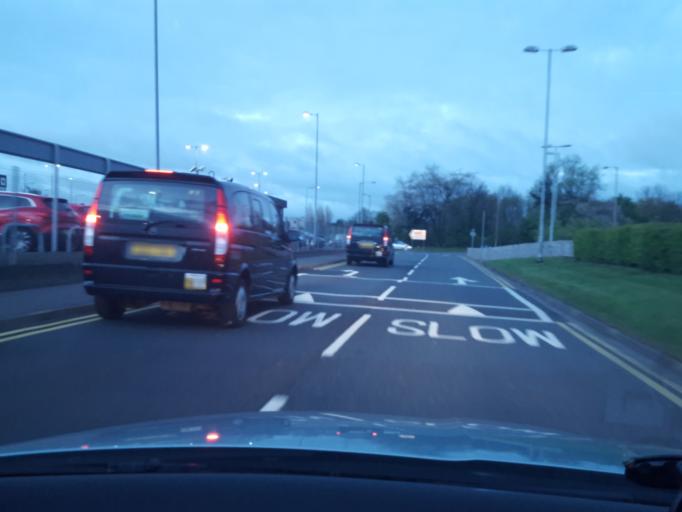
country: GB
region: Scotland
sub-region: Edinburgh
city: Ratho
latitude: 55.9459
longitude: -3.3609
